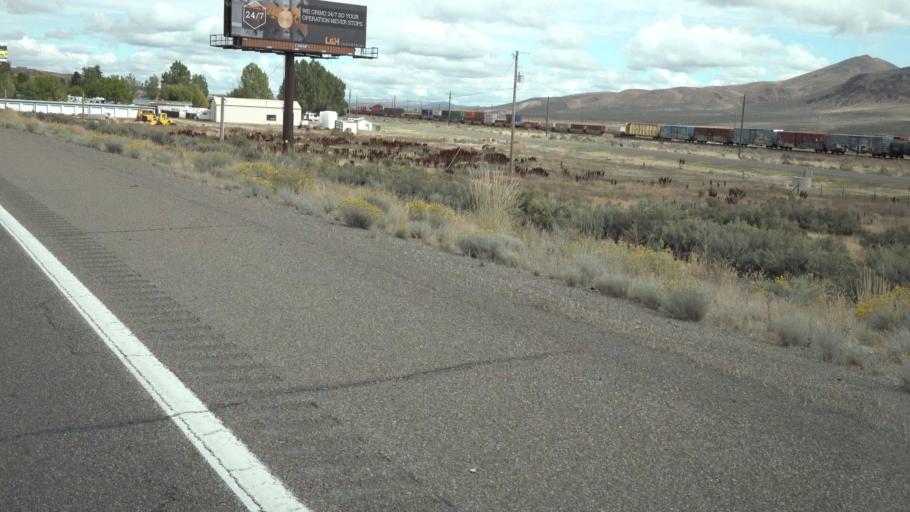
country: US
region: Nevada
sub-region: Elko County
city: Elko
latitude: 40.8841
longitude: -115.7145
